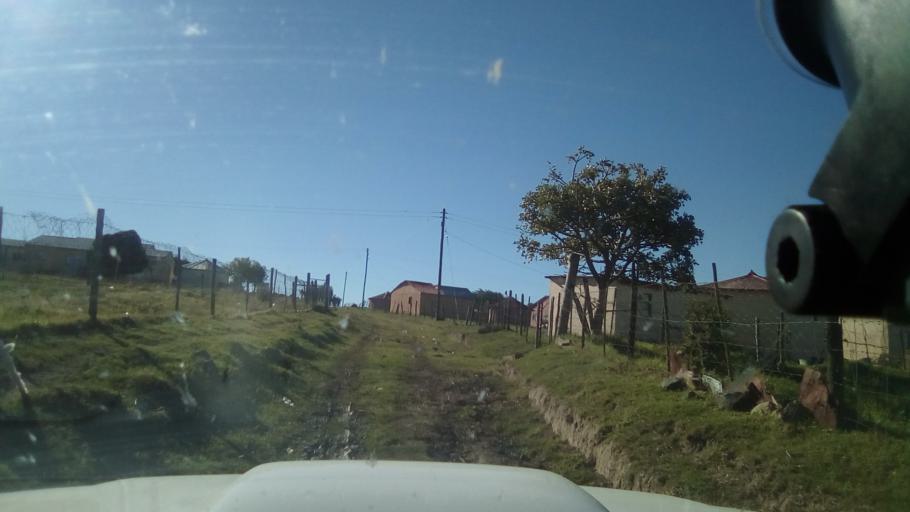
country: ZA
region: Eastern Cape
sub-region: Buffalo City Metropolitan Municipality
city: Bhisho
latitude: -32.9386
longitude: 27.2916
